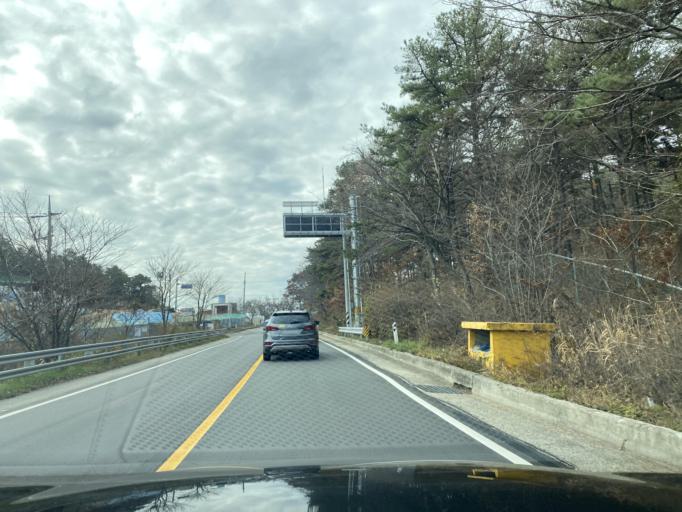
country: KR
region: Chungcheongnam-do
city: Hongsung
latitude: 36.6625
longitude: 126.6323
